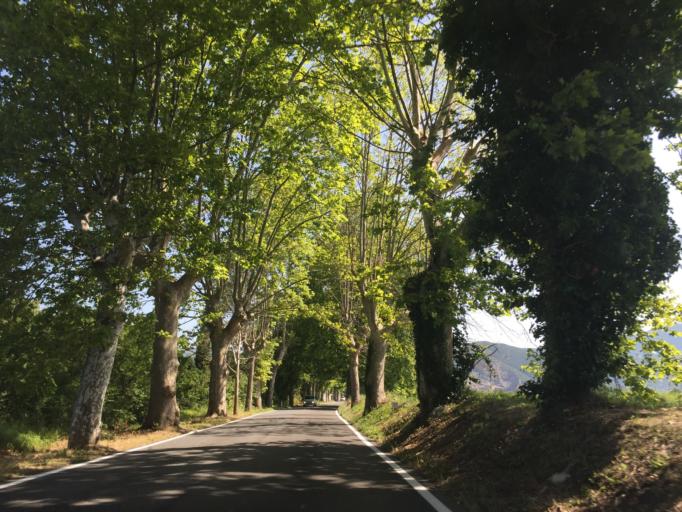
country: IT
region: Tuscany
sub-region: Province of Pisa
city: Gello
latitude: 43.7404
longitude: 10.4259
